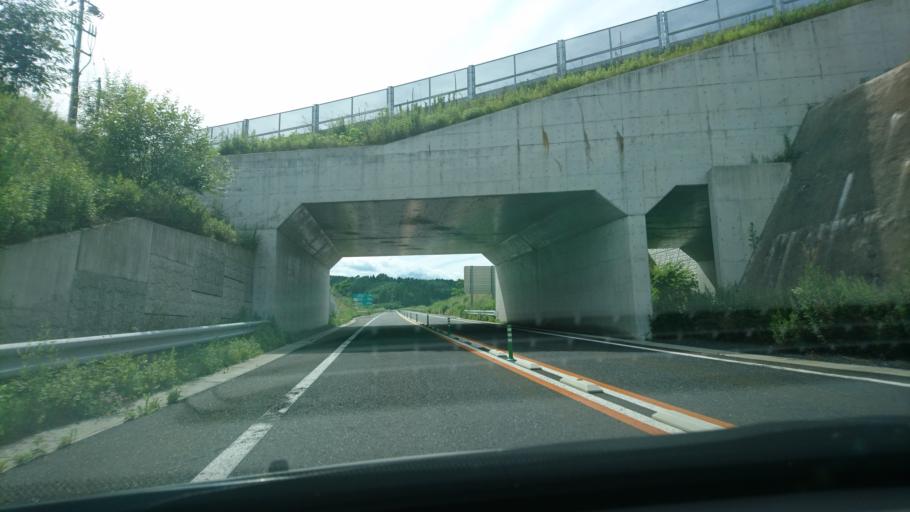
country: JP
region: Aomori
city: Hachinohe
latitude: 40.4793
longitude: 141.4953
